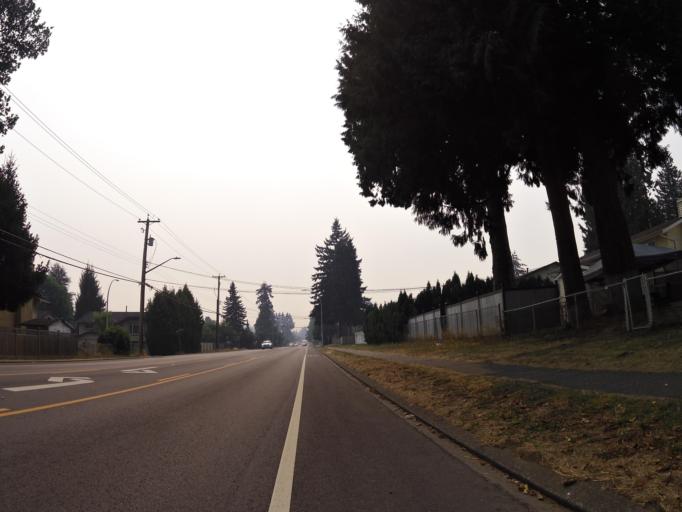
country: CA
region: British Columbia
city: Surrey
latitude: 49.1244
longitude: -122.8566
